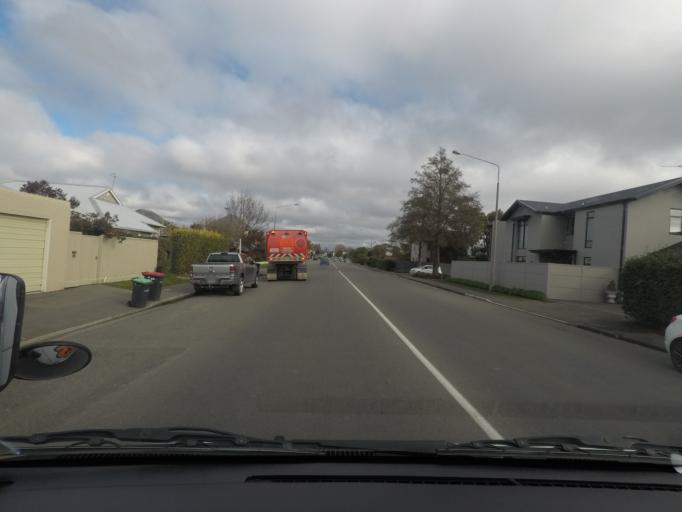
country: NZ
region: Canterbury
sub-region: Christchurch City
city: Christchurch
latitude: -43.5107
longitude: 172.6276
